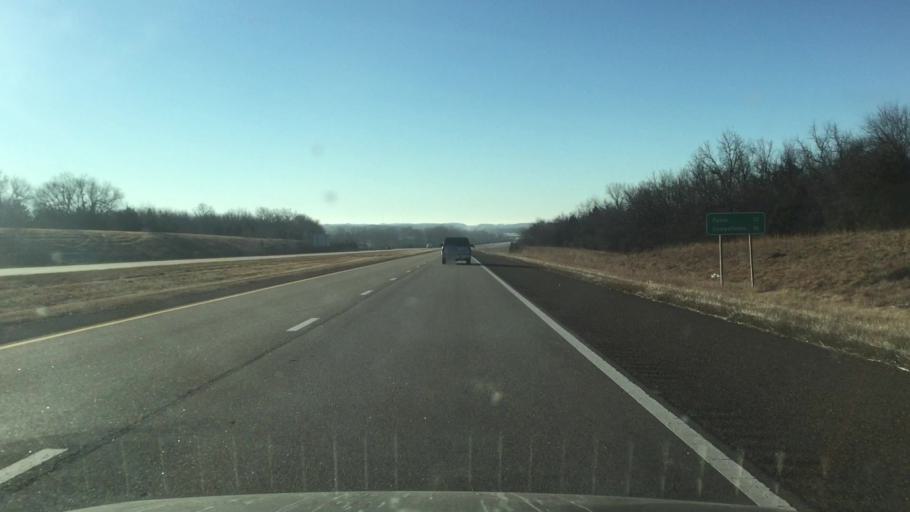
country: US
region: Kansas
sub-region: Johnson County
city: Spring Hill
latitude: 38.7129
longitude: -94.8347
